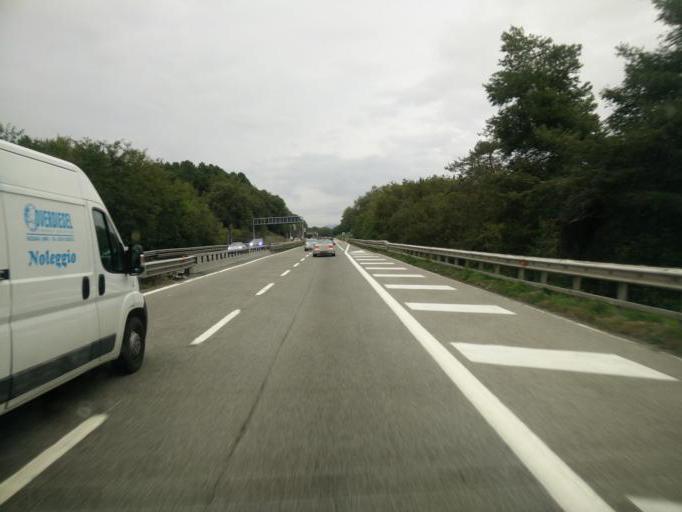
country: IT
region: Tuscany
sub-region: Province of Florence
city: Cavallina
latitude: 43.9899
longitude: 11.2150
